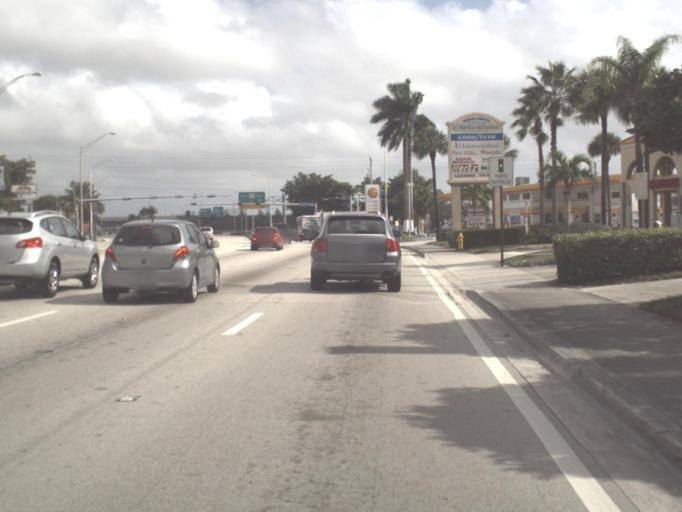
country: US
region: Florida
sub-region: Miami-Dade County
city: Virginia Gardens
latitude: 25.8094
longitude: -80.3268
